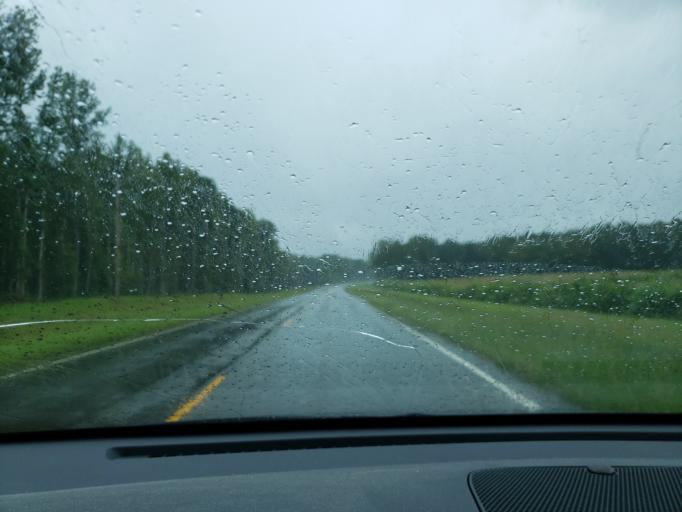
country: US
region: North Carolina
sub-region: Bladen County
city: Elizabethtown
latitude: 34.5213
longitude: -78.6517
